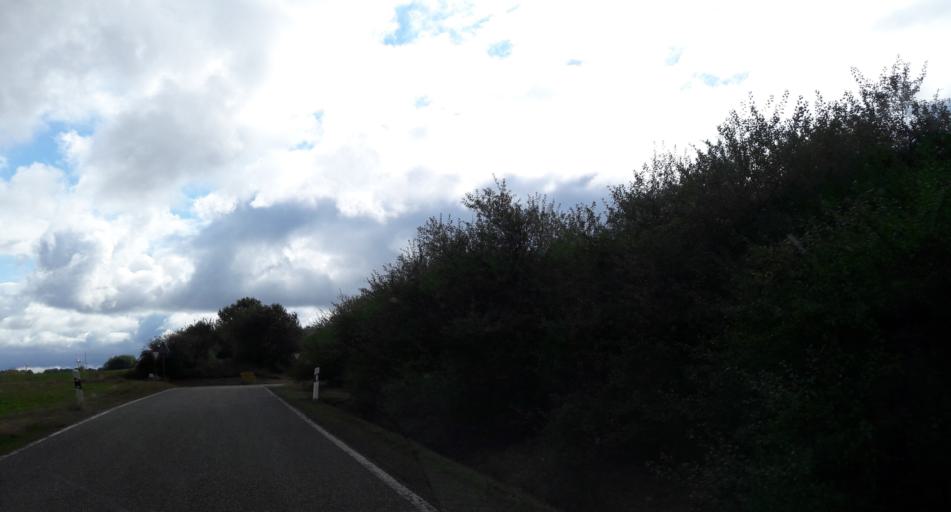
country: DE
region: Saarland
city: Freisen
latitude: 49.5269
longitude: 7.2238
